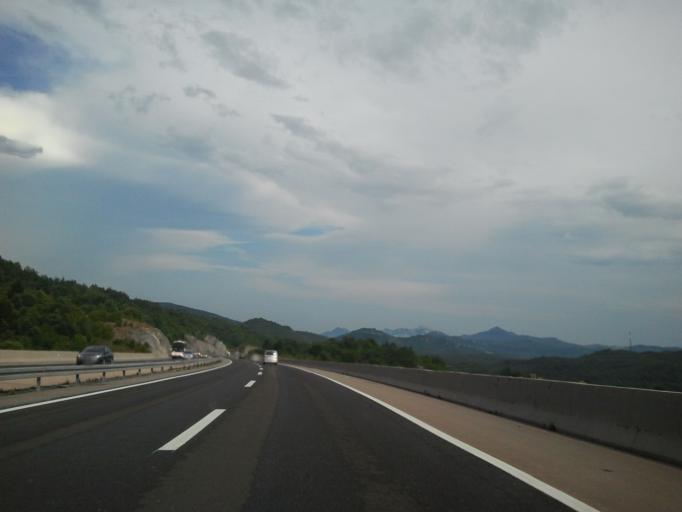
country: HR
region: Zadarska
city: Obrovac
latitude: 44.3327
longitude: 15.6593
